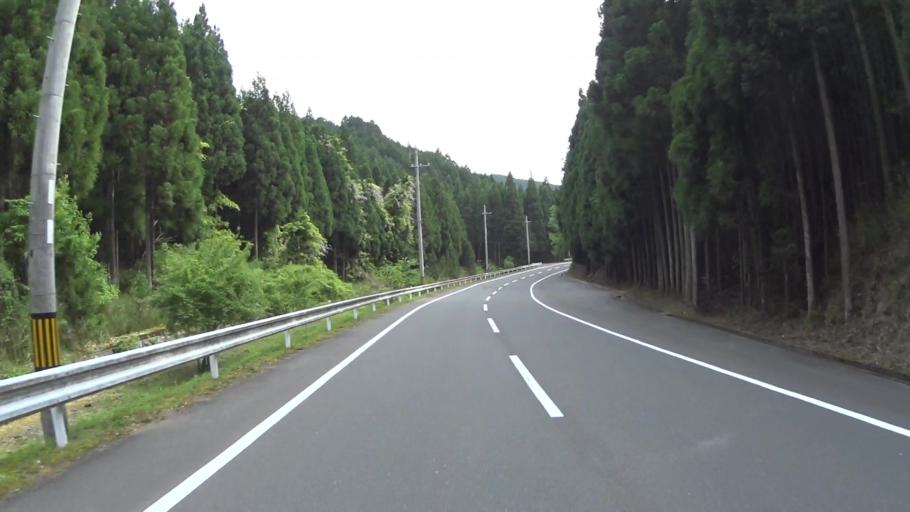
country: JP
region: Kyoto
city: Kameoka
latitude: 35.1482
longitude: 135.6191
